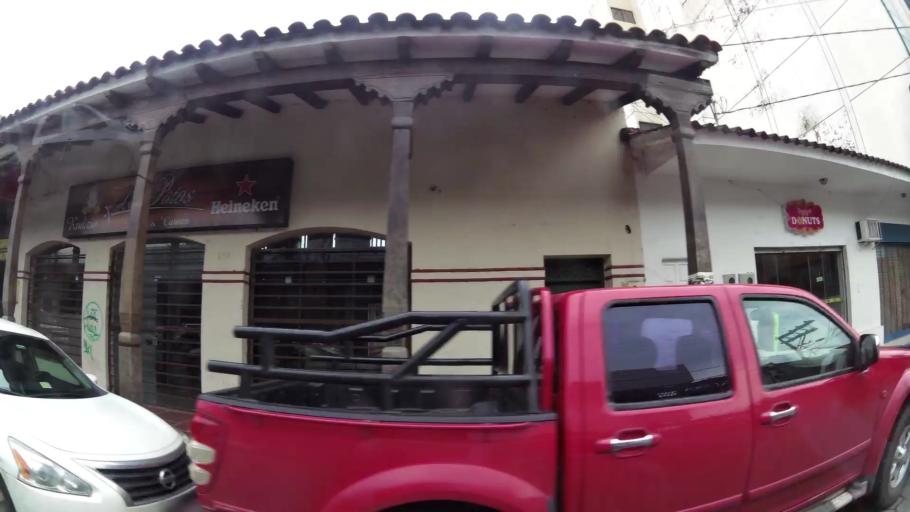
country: BO
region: Santa Cruz
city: Santa Cruz de la Sierra
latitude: -17.7768
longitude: -63.1821
